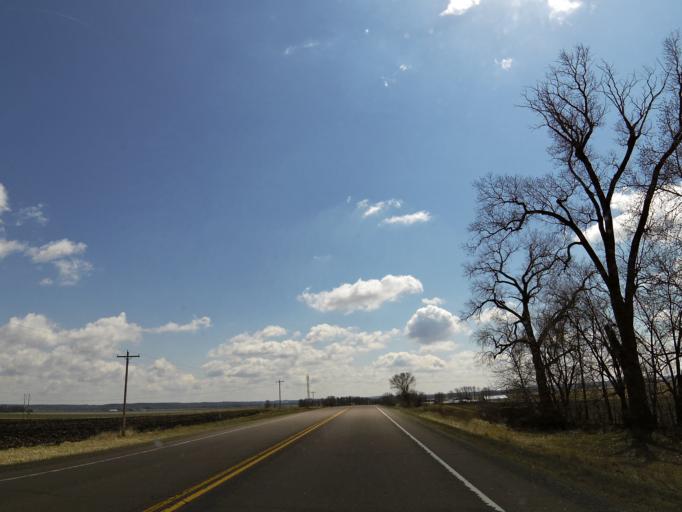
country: US
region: Minnesota
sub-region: Goodhue County
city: Cannon Falls
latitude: 44.5536
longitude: -92.9948
